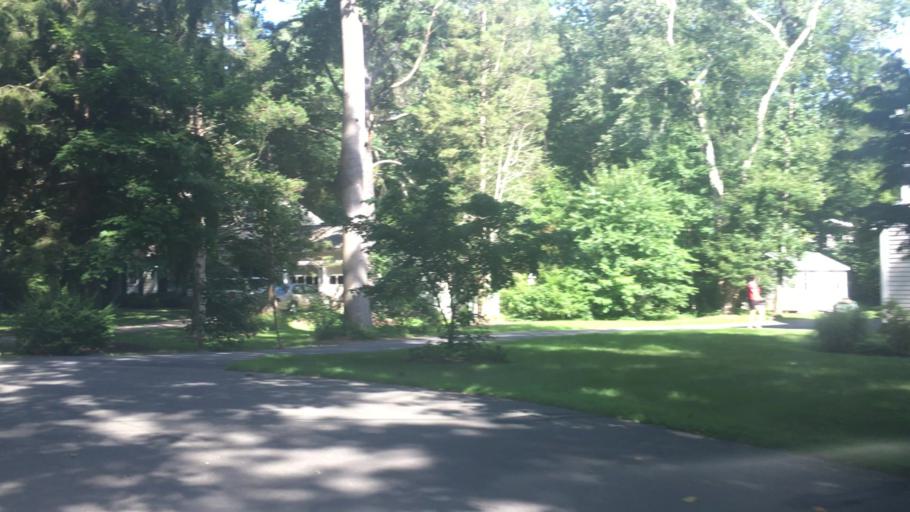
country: US
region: Connecticut
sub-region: Middlesex County
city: Essex Village
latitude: 41.3584
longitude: -72.4071
